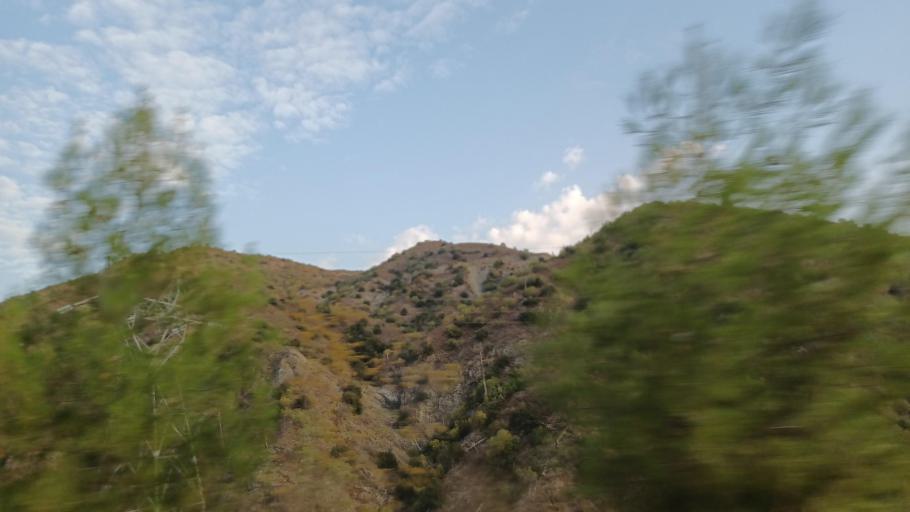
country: CY
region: Limassol
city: Pelendri
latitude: 34.8760
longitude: 32.9206
